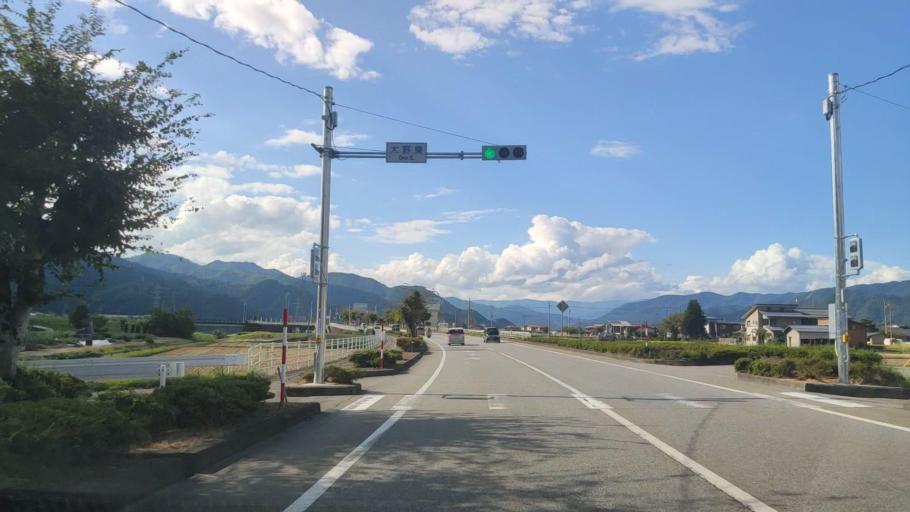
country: JP
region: Gifu
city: Takayama
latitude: 36.2157
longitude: 137.2041
